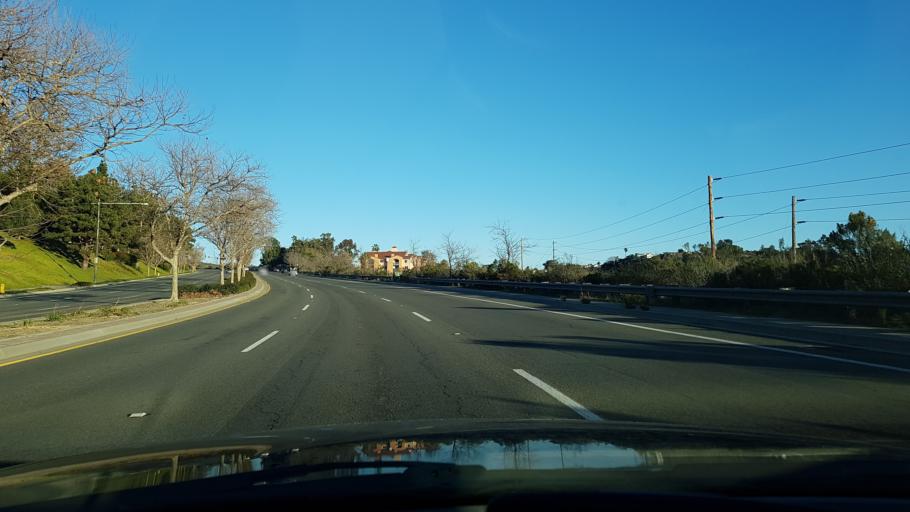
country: US
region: California
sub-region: San Diego County
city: La Jolla
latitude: 32.8639
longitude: -117.2056
